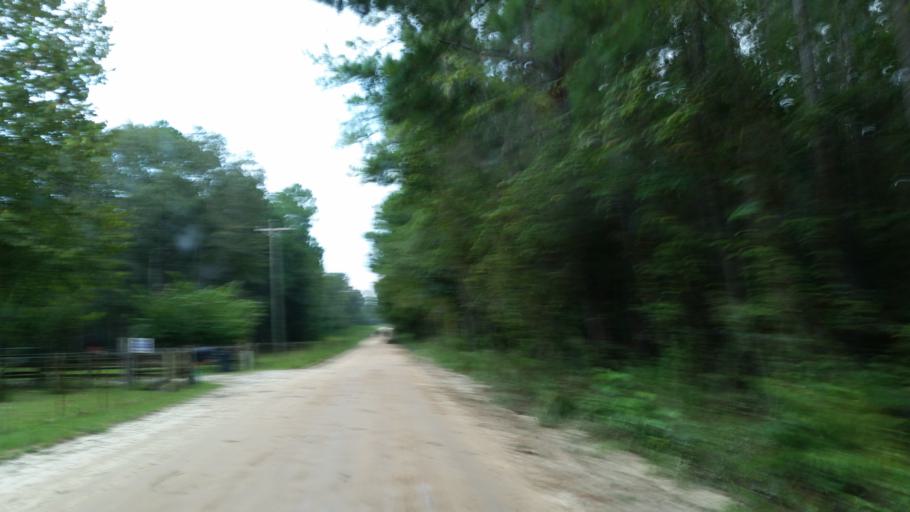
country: US
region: Georgia
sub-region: Lowndes County
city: Valdosta
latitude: 30.7215
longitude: -83.3055
